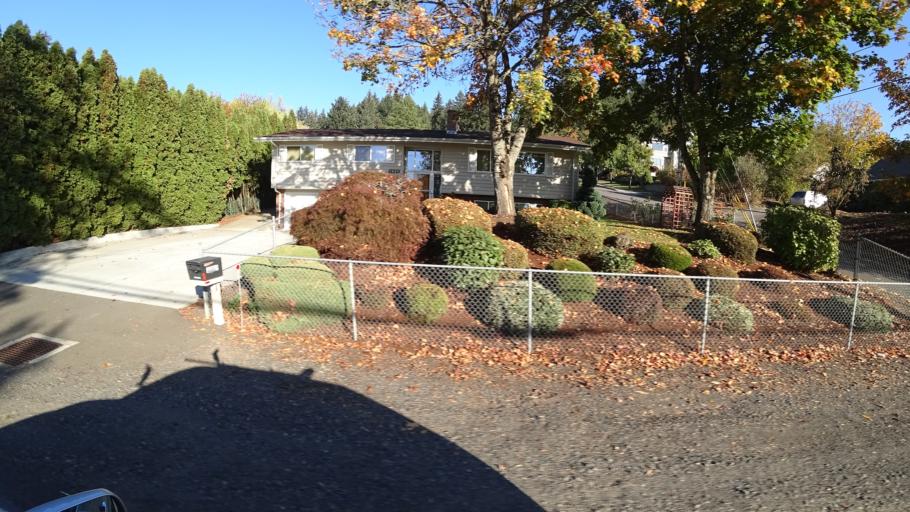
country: US
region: Oregon
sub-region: Multnomah County
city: Gresham
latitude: 45.4769
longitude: -122.4483
